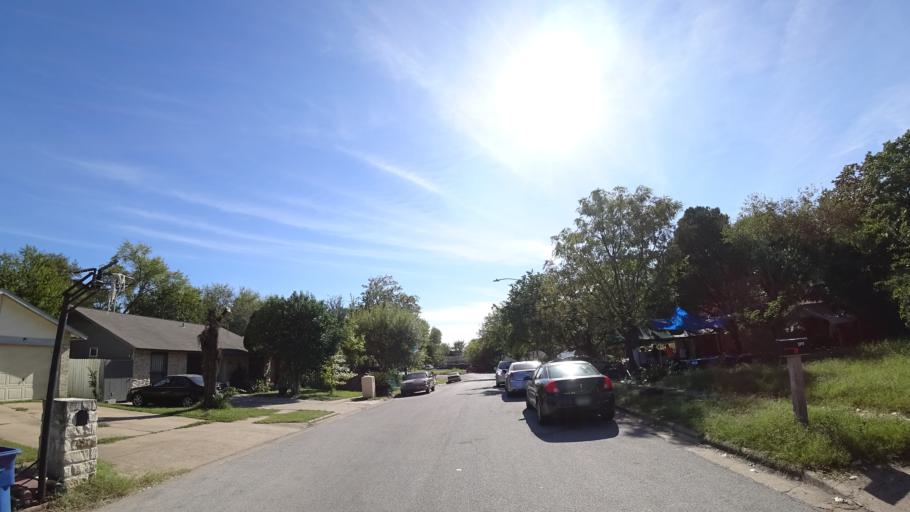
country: US
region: Texas
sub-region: Travis County
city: Austin
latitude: 30.1969
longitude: -97.7465
